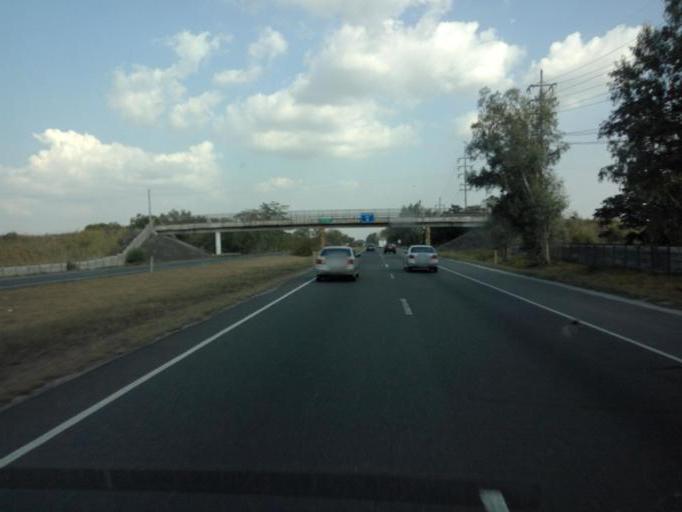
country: PH
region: Central Luzon
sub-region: Province of Pampanga
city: Culubasa
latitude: 15.1407
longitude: 120.6322
